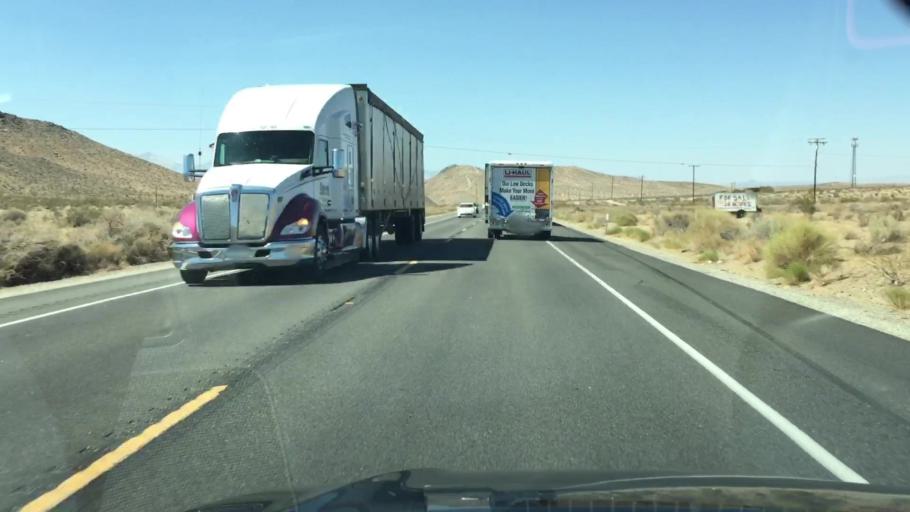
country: US
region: California
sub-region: Kern County
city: Ridgecrest
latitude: 35.5345
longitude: -117.6831
